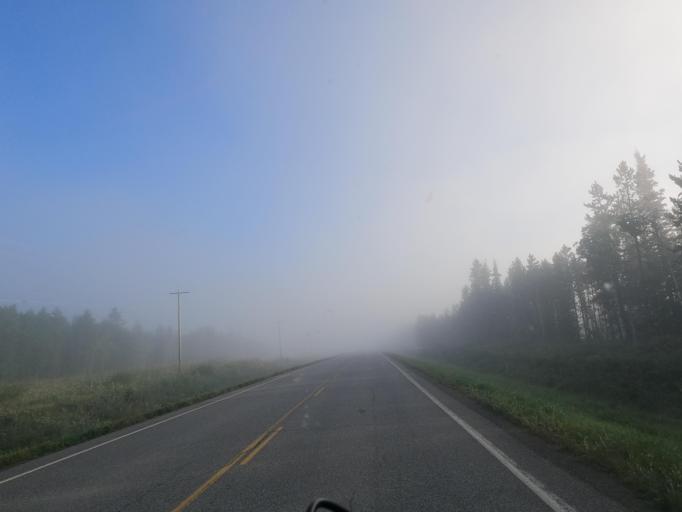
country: CA
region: Yukon
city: Whitehorse
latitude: 60.8852
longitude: -135.1854
